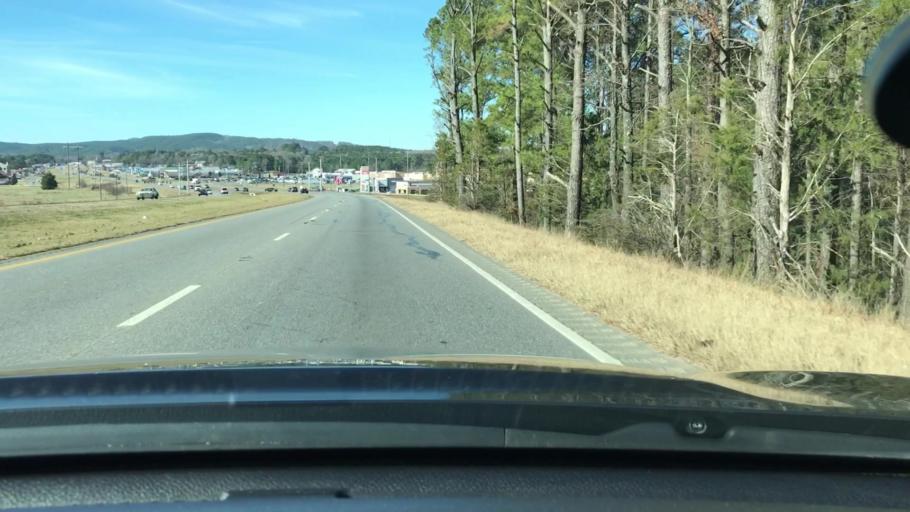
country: US
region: Alabama
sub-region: Talladega County
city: Mignon
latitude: 33.1694
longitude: -86.2804
